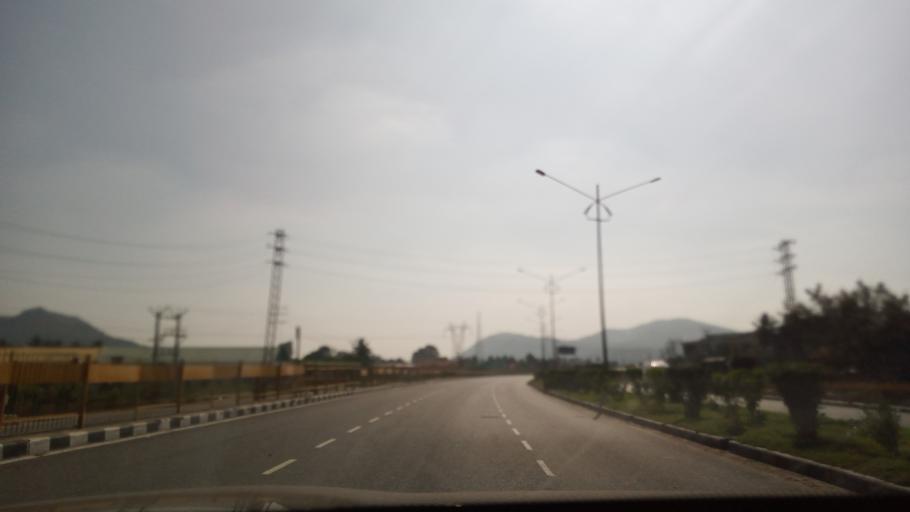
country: IN
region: Tamil Nadu
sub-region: Krishnagiri
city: Krishnagiri
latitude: 12.5121
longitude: 78.2292
